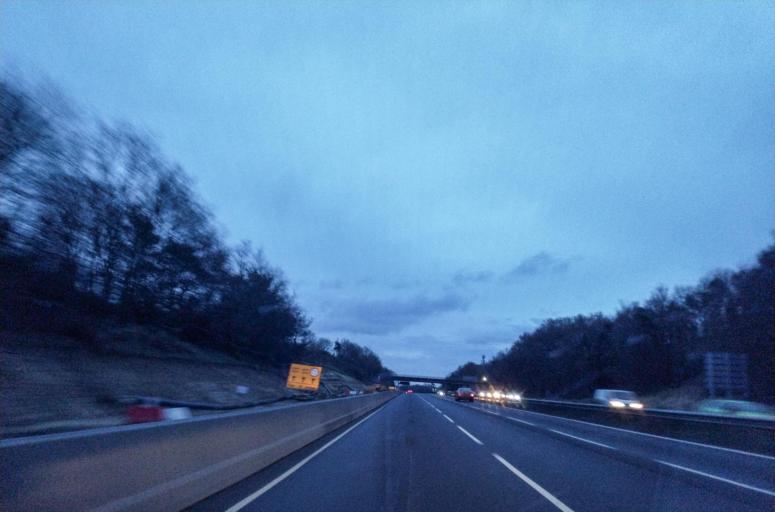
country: GB
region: England
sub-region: Kent
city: Larkfield
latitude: 51.3055
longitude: 0.4385
